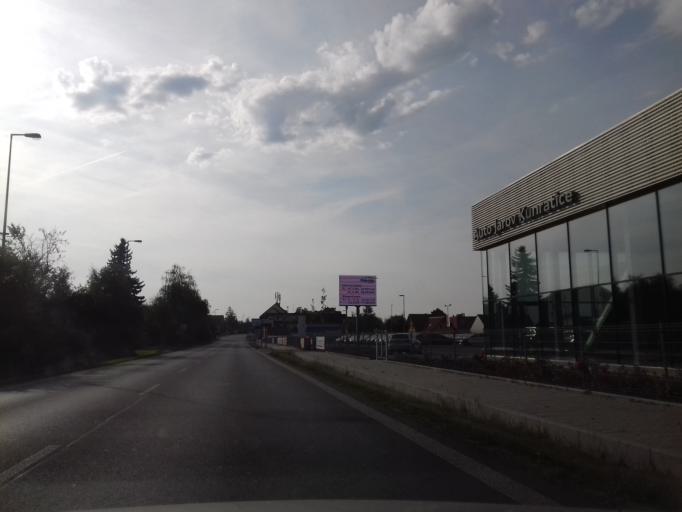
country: CZ
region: Central Bohemia
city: Vestec
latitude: 50.0099
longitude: 14.4779
